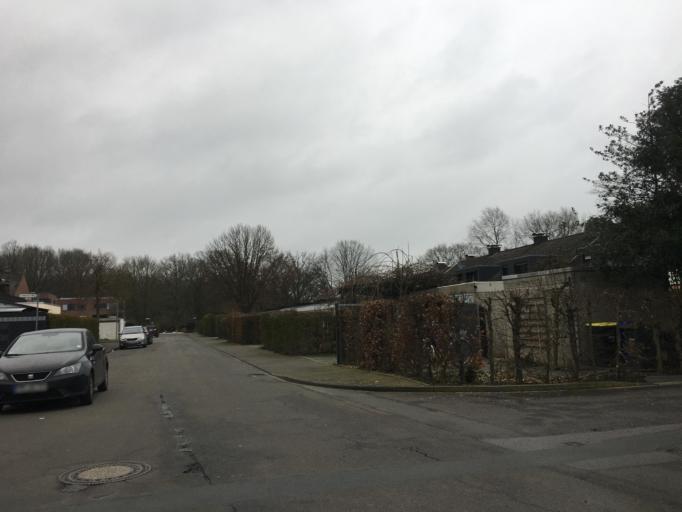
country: DE
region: North Rhine-Westphalia
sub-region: Regierungsbezirk Munster
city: Senden
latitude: 51.8561
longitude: 7.4683
